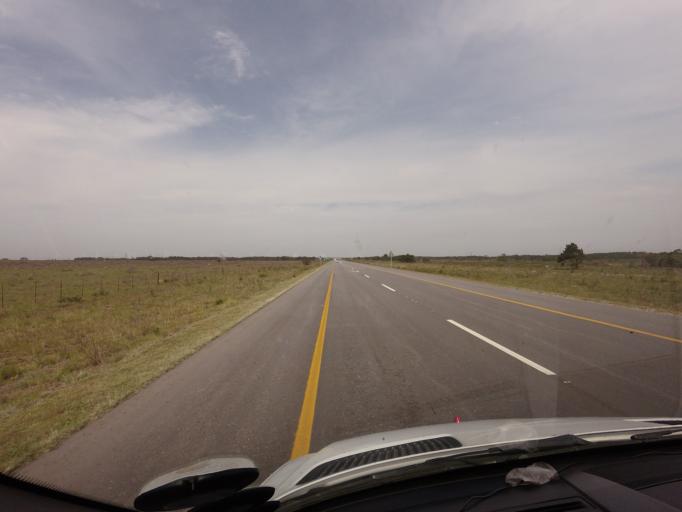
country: ZA
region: Eastern Cape
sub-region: Cacadu District Municipality
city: Kruisfontein
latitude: -34.0039
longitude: 24.7697
